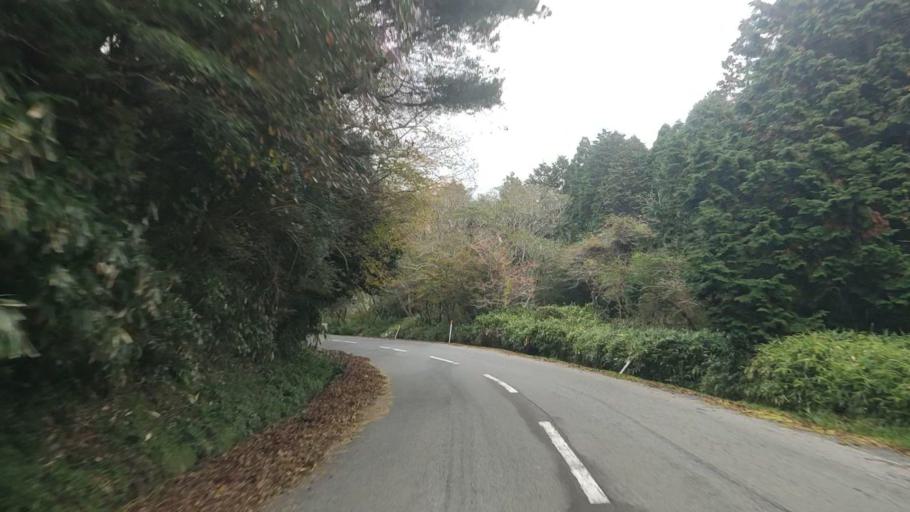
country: JP
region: Shizuoka
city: Heda
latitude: 34.9297
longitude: 138.8397
